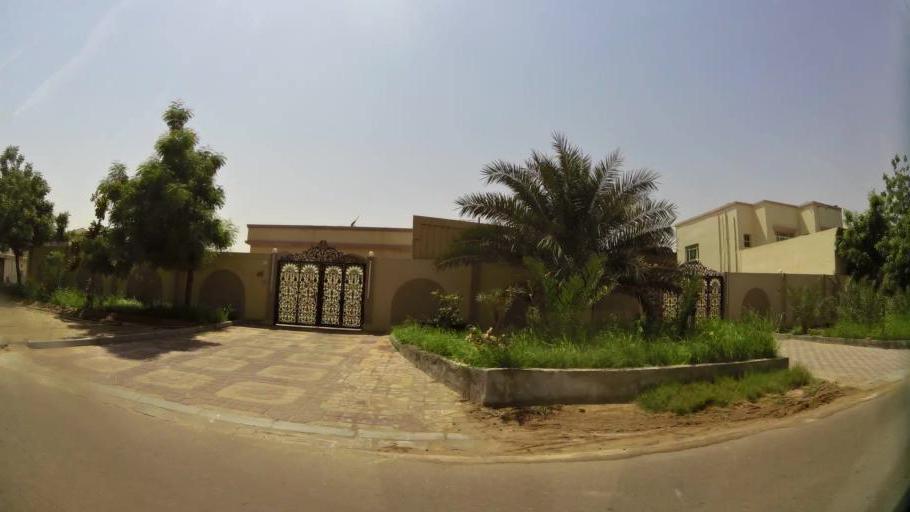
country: AE
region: Ajman
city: Ajman
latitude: 25.4240
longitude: 55.5202
